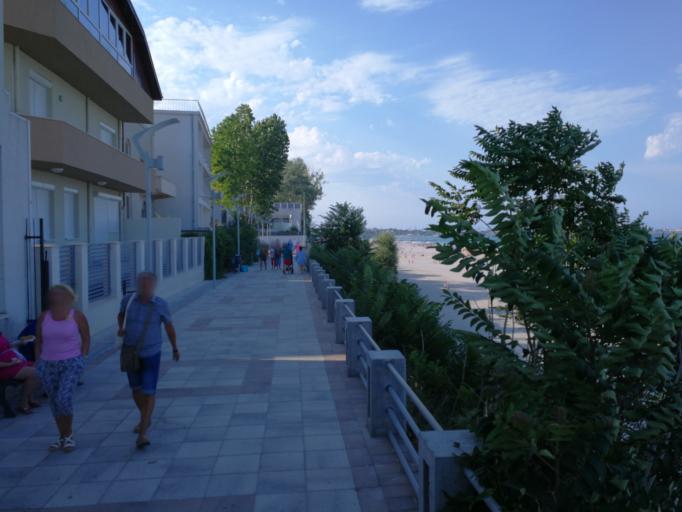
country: RO
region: Constanta
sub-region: Oras Eforie
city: Eforie Nord
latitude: 44.0657
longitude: 28.6392
